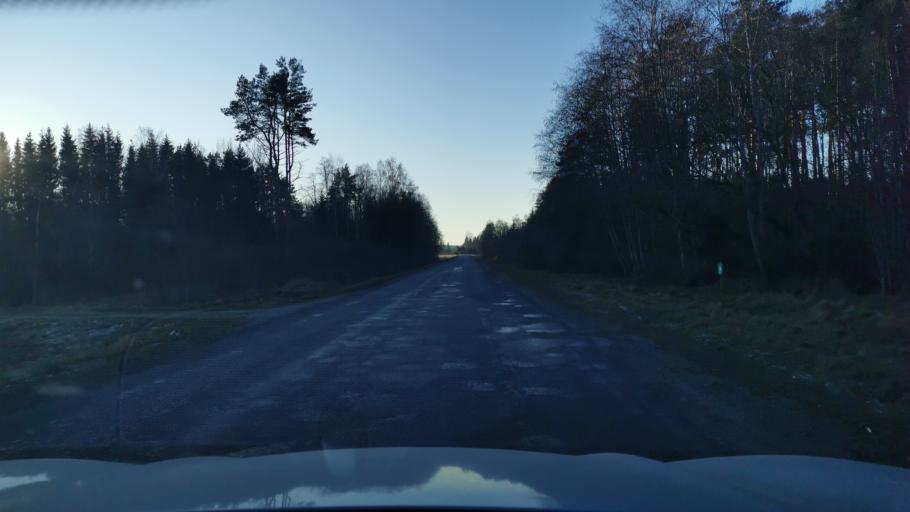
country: EE
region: Ida-Virumaa
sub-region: Kivioli linn
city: Kivioli
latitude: 59.3141
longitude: 27.0039
